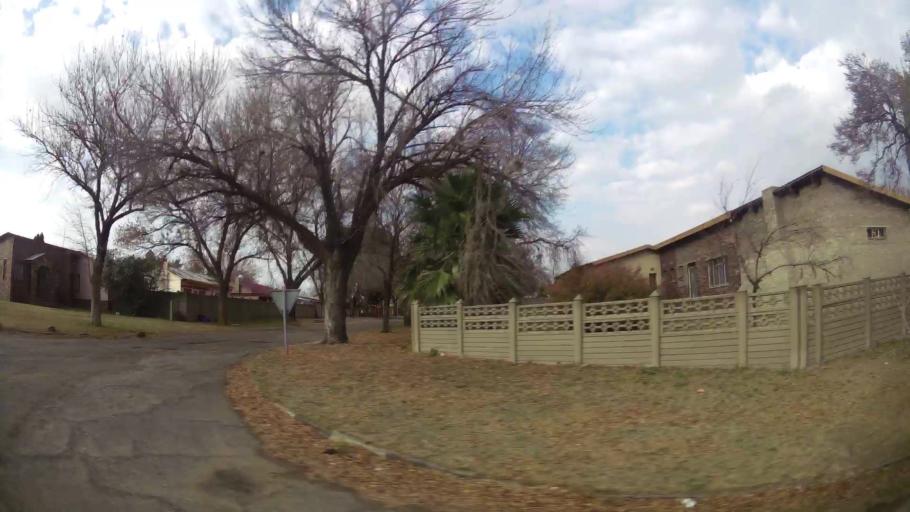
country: ZA
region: Orange Free State
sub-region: Fezile Dabi District Municipality
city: Sasolburg
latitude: -26.8251
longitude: 27.8272
